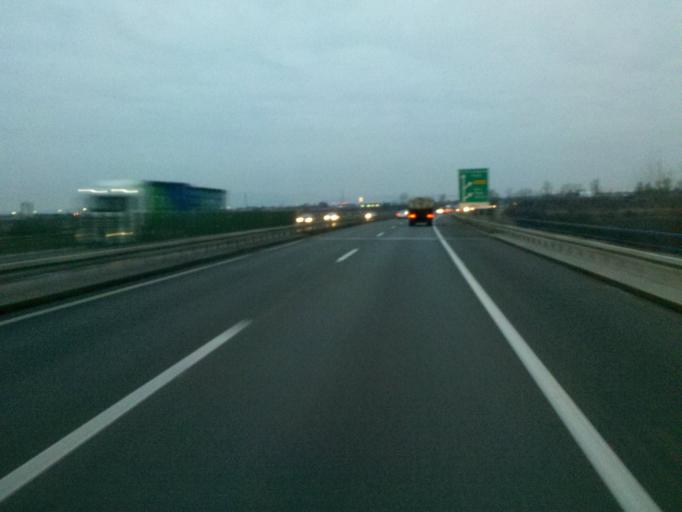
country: HR
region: Grad Zagreb
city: Zadvorsko
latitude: 45.7493
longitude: 15.9170
